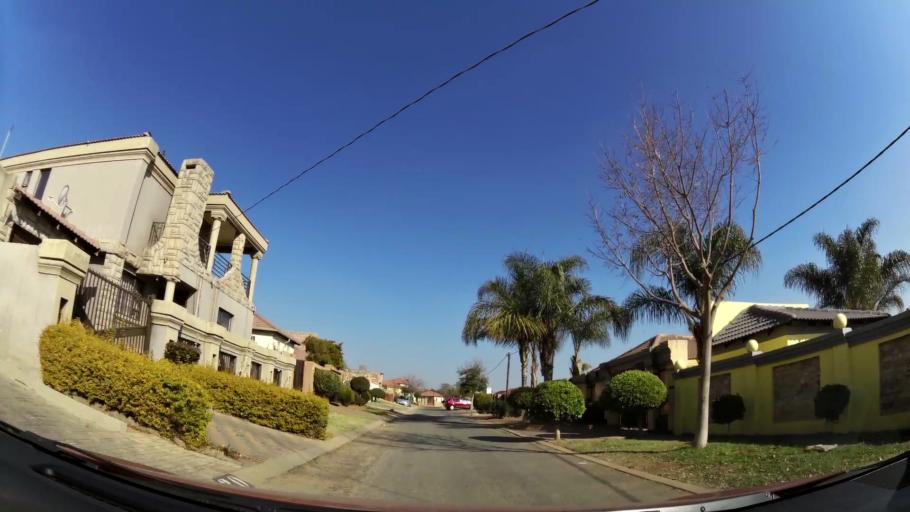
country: ZA
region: Gauteng
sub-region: West Rand District Municipality
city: Muldersdriseloop
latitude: -26.0431
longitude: 27.9216
